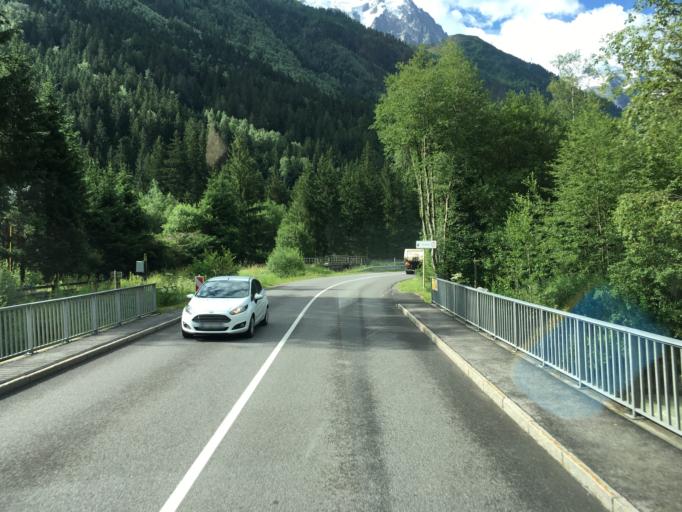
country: FR
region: Rhone-Alpes
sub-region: Departement de la Haute-Savoie
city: Chamonix-Mont-Blanc
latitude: 45.9355
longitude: 6.8891
